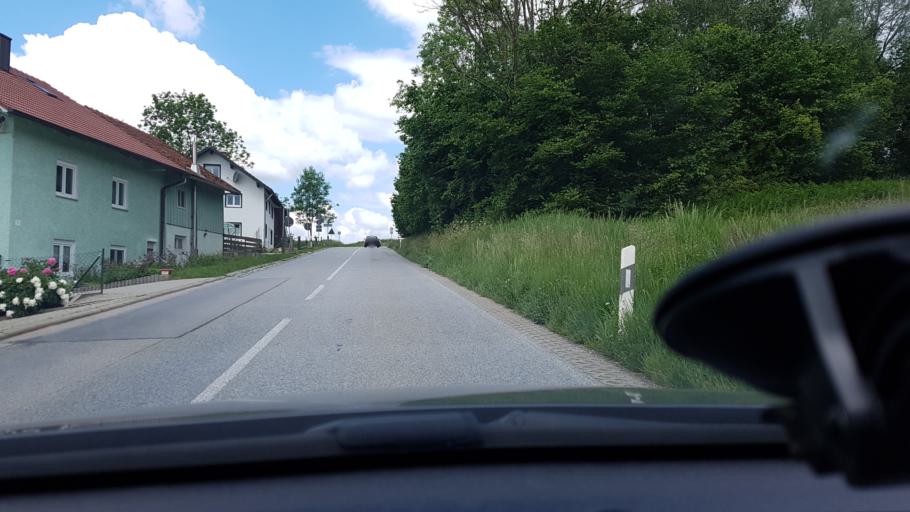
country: DE
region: Bavaria
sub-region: Lower Bavaria
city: Kirchham
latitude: 48.3520
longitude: 13.2454
